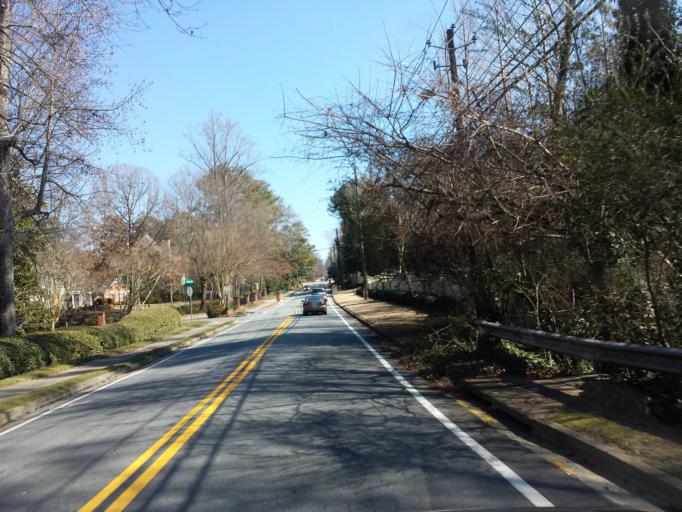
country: US
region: Georgia
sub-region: Fulton County
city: Sandy Springs
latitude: 33.9194
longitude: -84.4131
